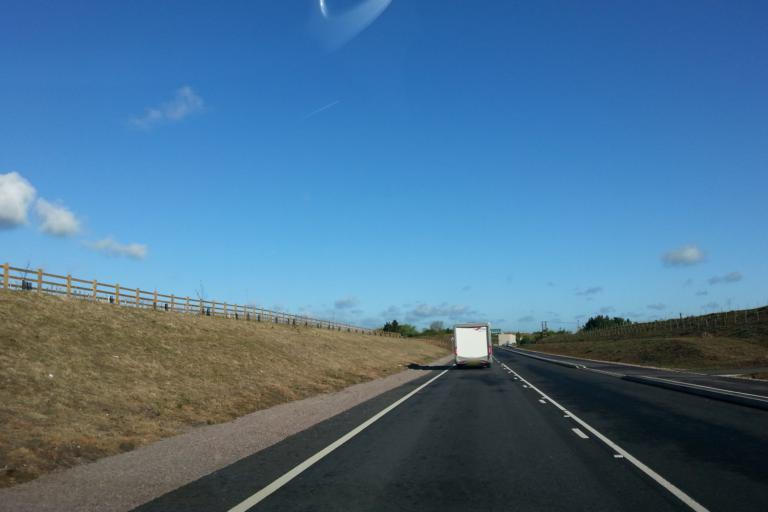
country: GB
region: England
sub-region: Nottinghamshire
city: Newark on Trent
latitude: 53.0481
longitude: -0.7974
